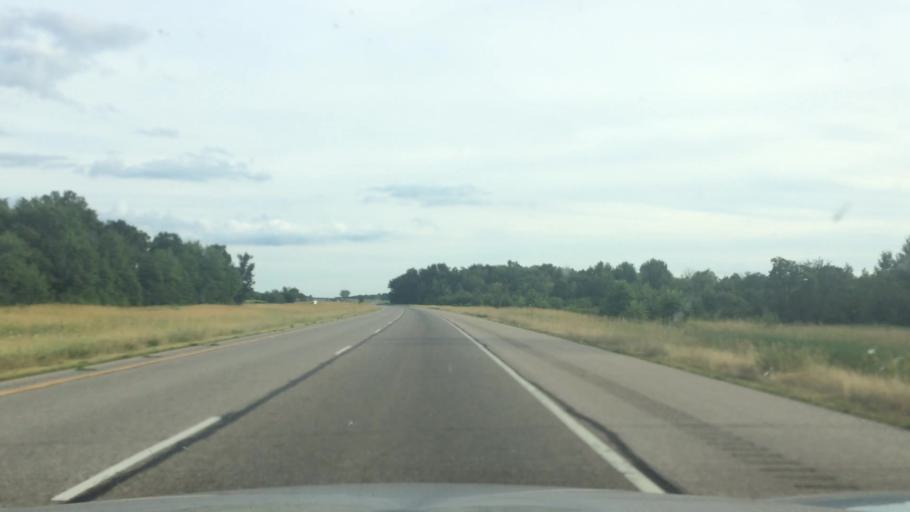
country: US
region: Wisconsin
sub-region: Waushara County
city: Wautoma
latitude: 44.1706
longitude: -89.5323
